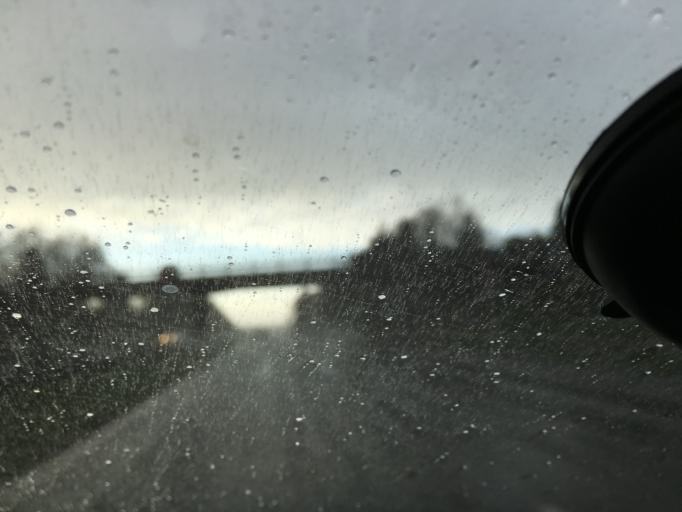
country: DK
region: Central Jutland
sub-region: Randers Kommune
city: Randers
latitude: 56.4382
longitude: 10.0202
